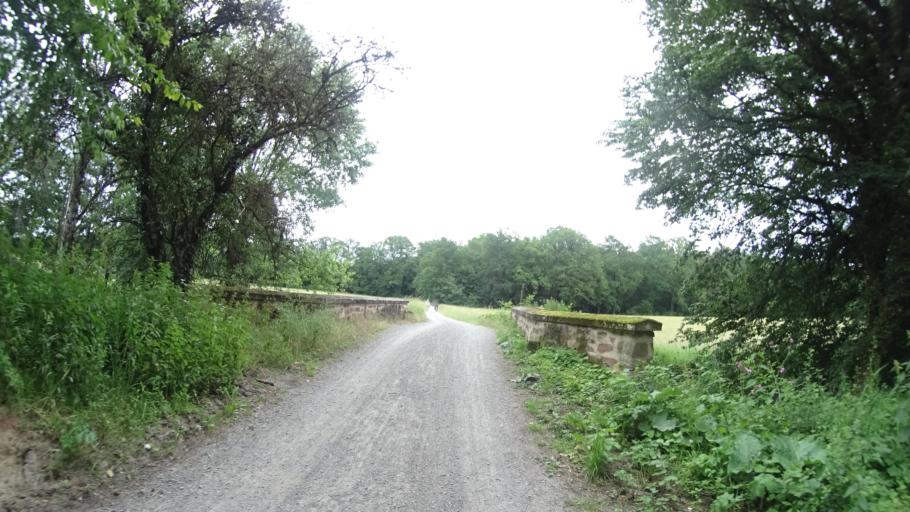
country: DE
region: Baden-Wuerttemberg
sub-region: Karlsruhe Region
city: Rheinstetten
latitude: 48.9643
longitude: 8.3576
